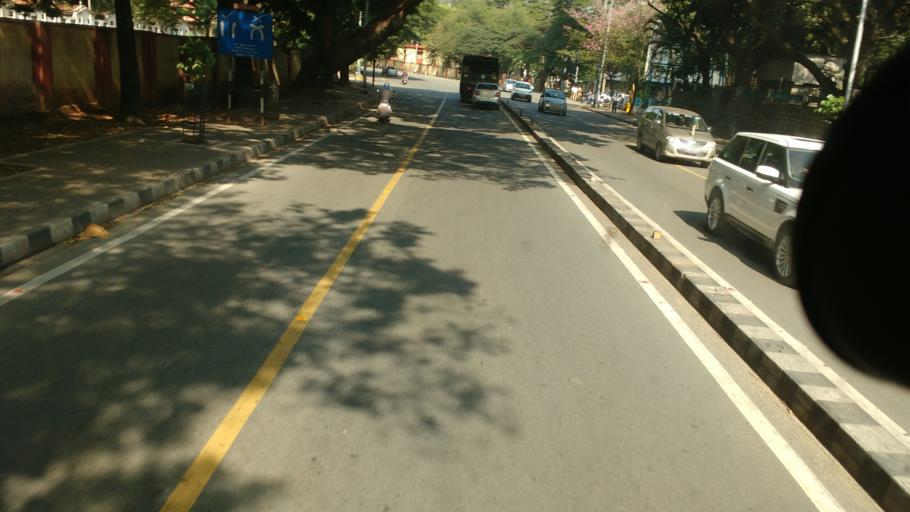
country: IN
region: Karnataka
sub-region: Bangalore Urban
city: Bangalore
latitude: 12.9651
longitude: 77.6255
